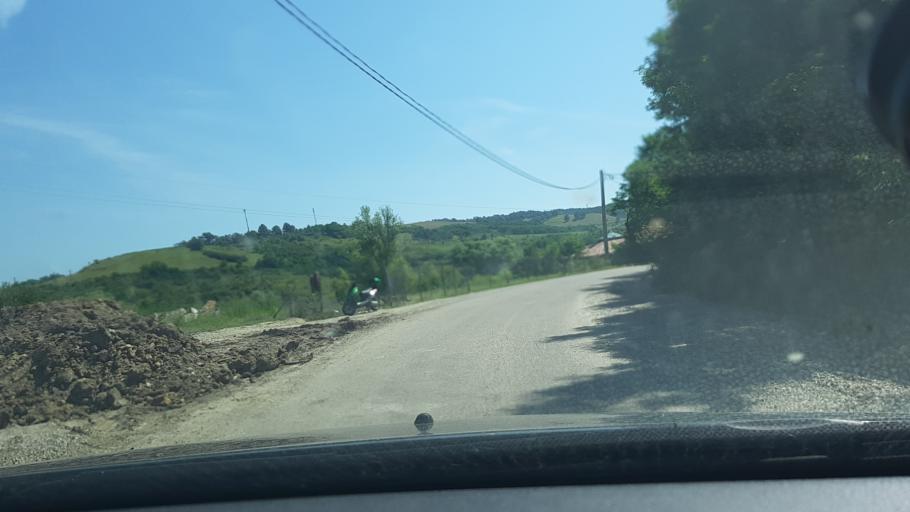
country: RO
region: Hunedoara
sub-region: Comuna Teliucu Inferior
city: Teliucu Inferior
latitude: 45.6898
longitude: 22.8666
